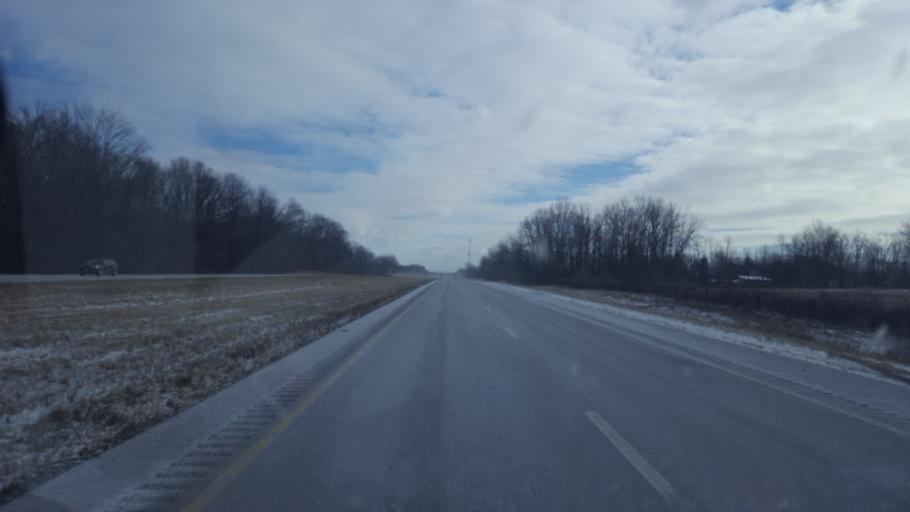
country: US
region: Ohio
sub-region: Licking County
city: Etna
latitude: 39.9467
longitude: -82.6409
